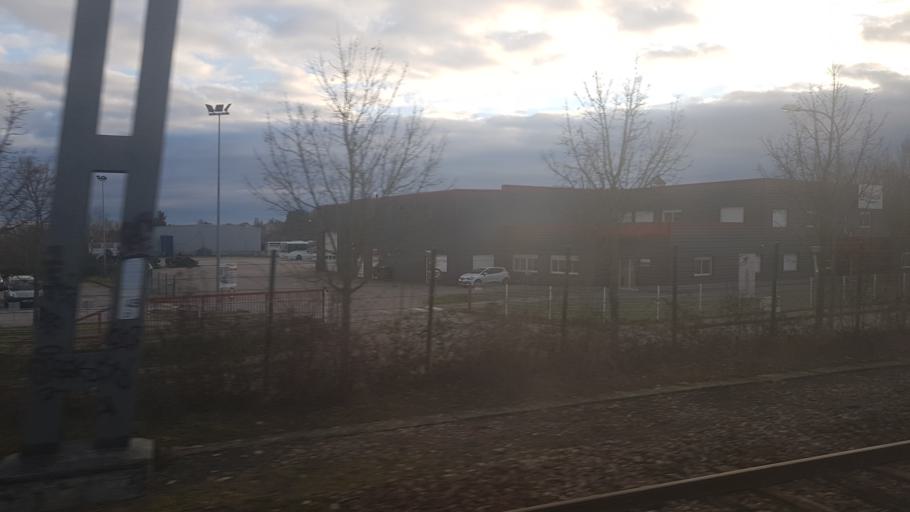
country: FR
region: Lorraine
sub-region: Departement des Vosges
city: Golbey
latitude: 48.1898
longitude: 6.4375
